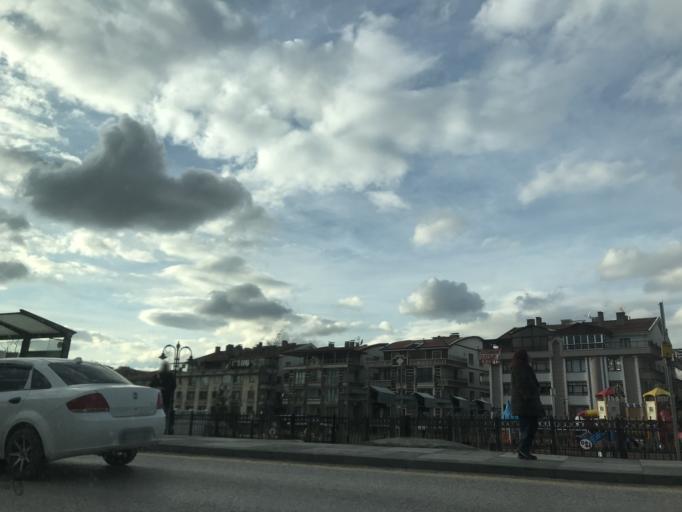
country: TR
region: Ankara
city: Mamak
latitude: 39.9827
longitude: 32.8866
